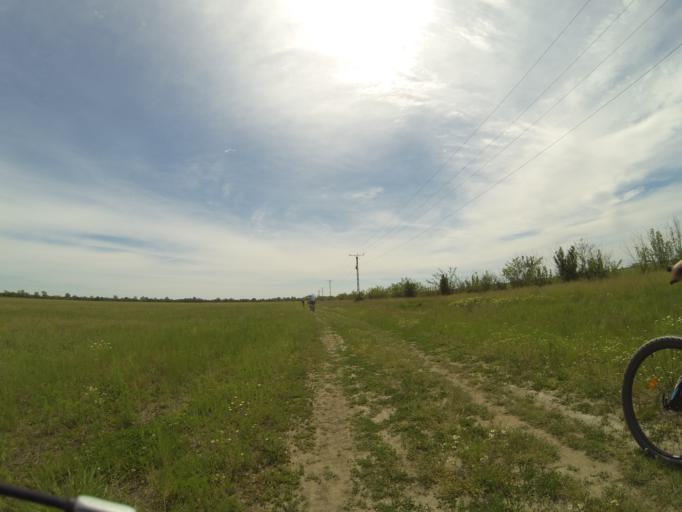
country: RO
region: Dolj
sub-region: Comuna Leu
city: Leu
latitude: 44.2022
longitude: 23.9726
